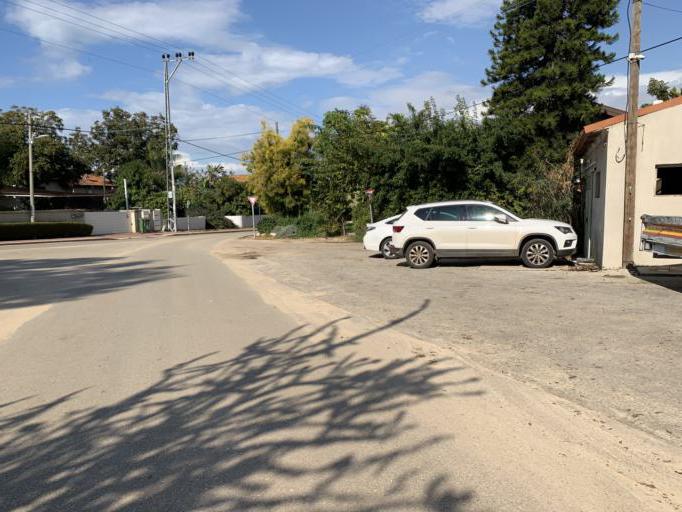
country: IL
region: Central District
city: Ra'anana
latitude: 32.1681
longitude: 34.8755
